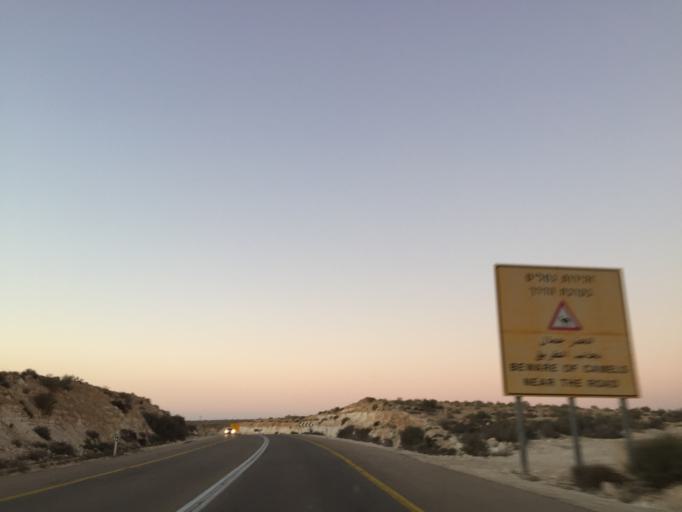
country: IL
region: Southern District
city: Midreshet Ben-Gurion
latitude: 30.8899
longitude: 34.7922
